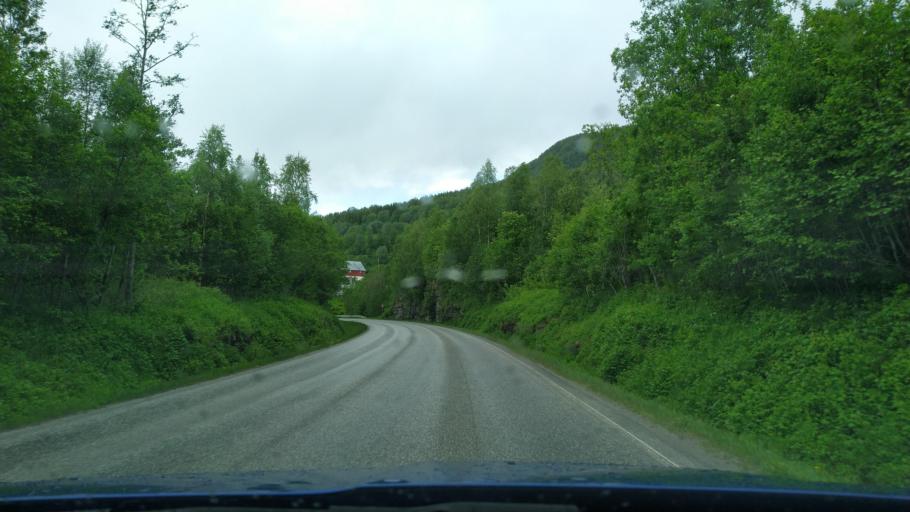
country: NO
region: Troms
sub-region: Sorreisa
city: Sorreisa
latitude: 69.1571
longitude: 18.1605
